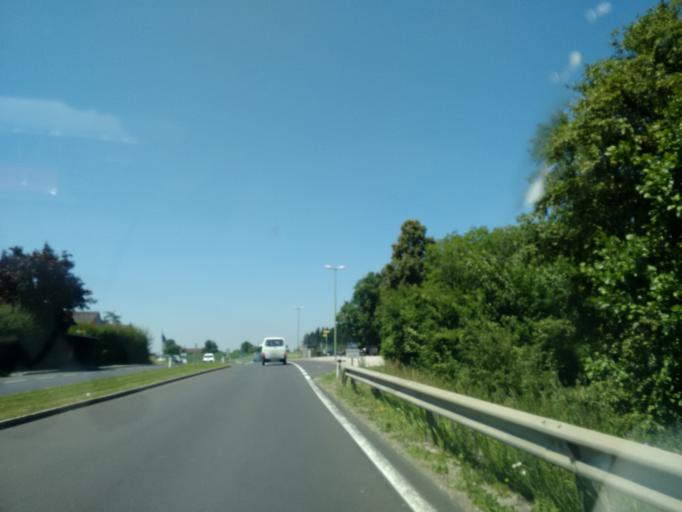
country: AT
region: Upper Austria
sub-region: Wels-Land
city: Buchkirchen
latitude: 48.1925
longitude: 14.0025
